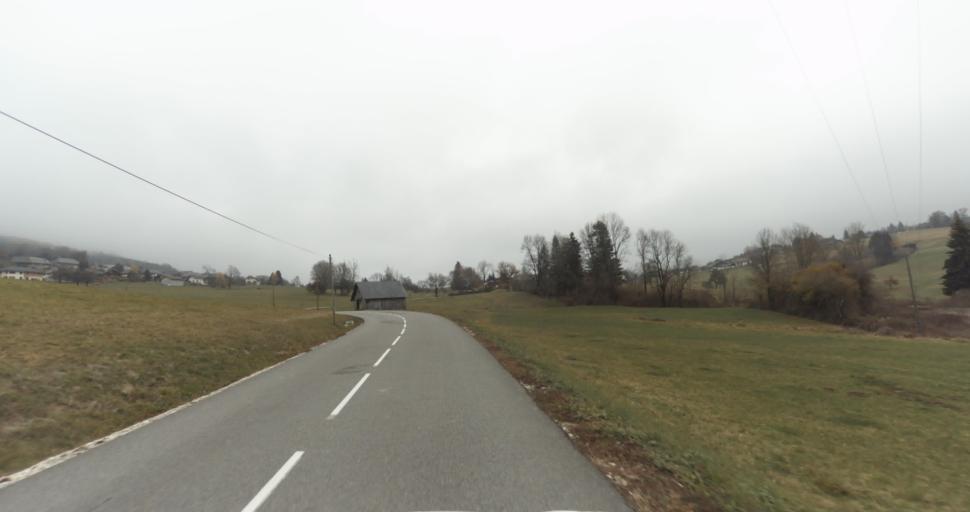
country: FR
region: Rhone-Alpes
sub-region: Departement de la Haute-Savoie
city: Gruffy
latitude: 45.7675
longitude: 6.1270
